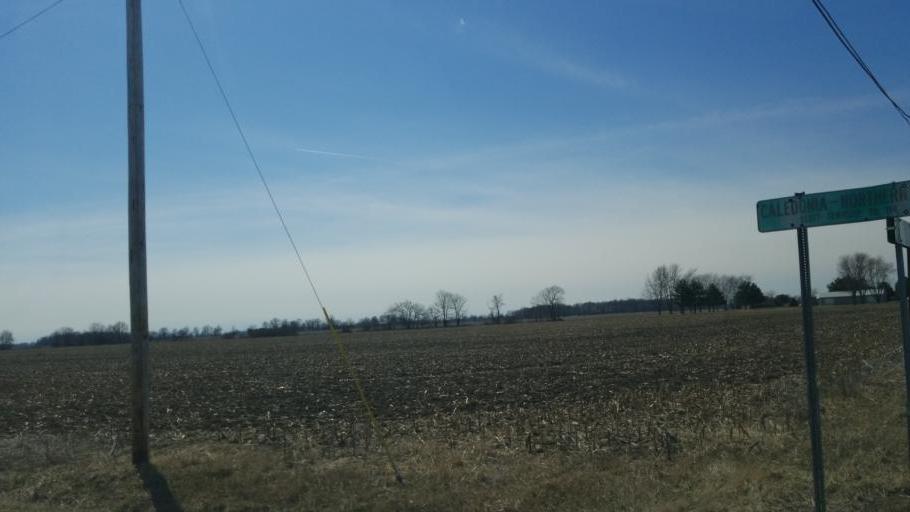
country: US
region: Ohio
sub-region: Crawford County
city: Bucyrus
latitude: 40.6742
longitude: -82.9698
